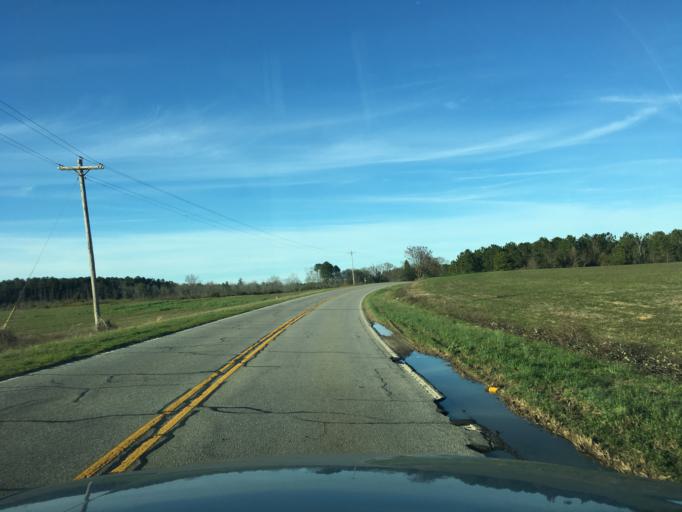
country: US
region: South Carolina
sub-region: Lexington County
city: Batesburg
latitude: 33.7917
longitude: -81.6442
